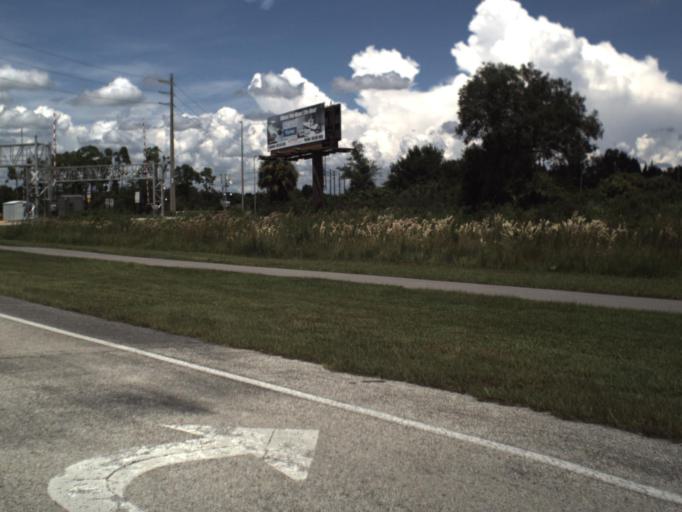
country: US
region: Florida
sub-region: Charlotte County
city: Charlotte Park
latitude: 26.8907
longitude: -82.0228
